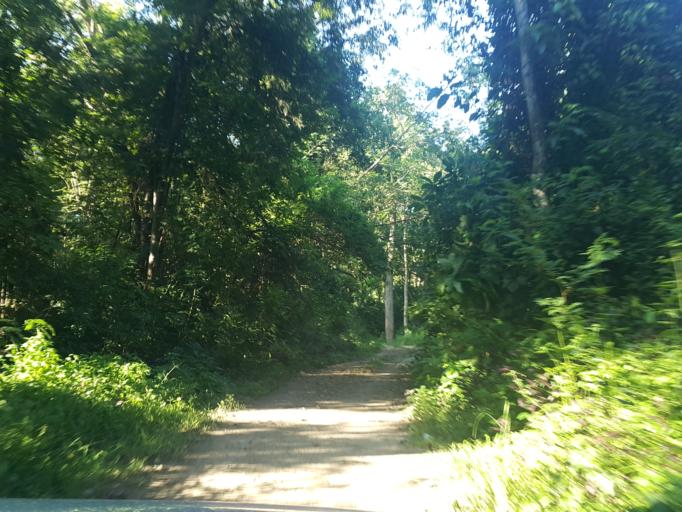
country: TH
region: Chiang Mai
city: Mae On
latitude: 18.7076
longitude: 99.2033
